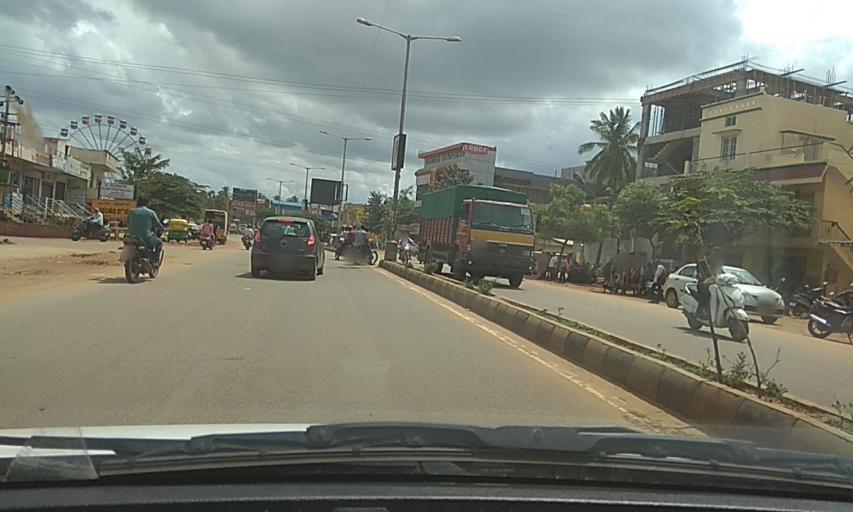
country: IN
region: Karnataka
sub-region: Tumkur
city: Tumkur
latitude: 13.3292
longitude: 77.0943
